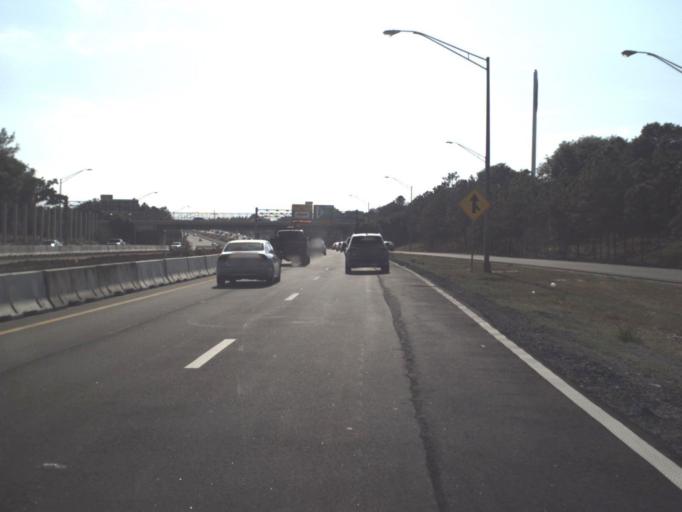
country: US
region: Florida
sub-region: Orange County
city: Orlovista
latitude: 28.5490
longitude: -81.4806
